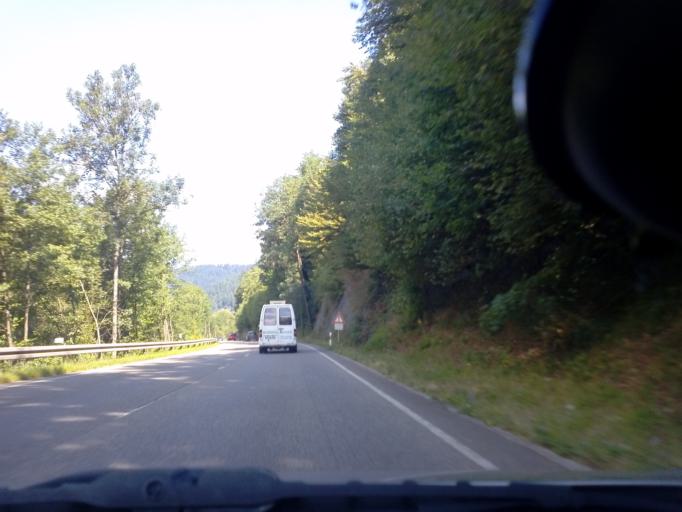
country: DE
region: Baden-Wuerttemberg
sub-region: Freiburg Region
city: Hausach
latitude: 48.2742
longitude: 8.1982
